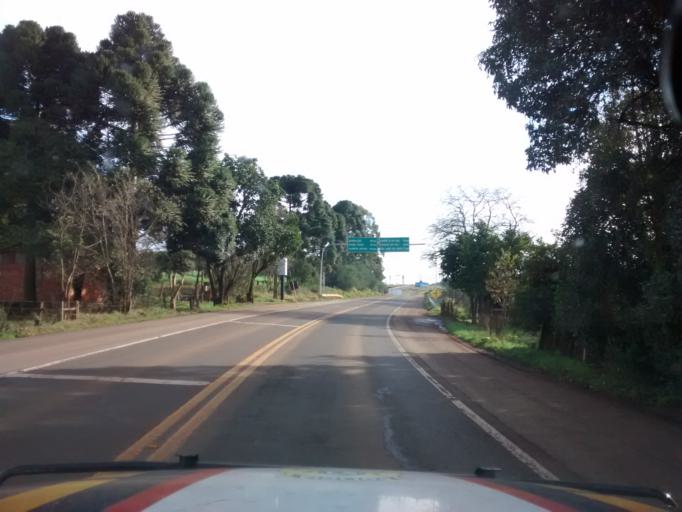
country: BR
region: Rio Grande do Sul
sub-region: Lagoa Vermelha
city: Lagoa Vermelha
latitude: -28.1935
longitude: -51.5256
